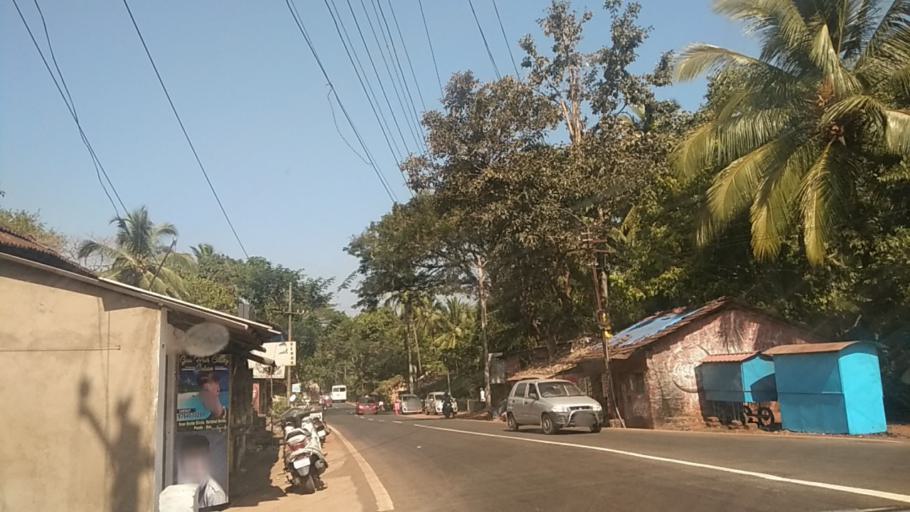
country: IN
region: Goa
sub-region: North Goa
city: Queula
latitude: 15.3542
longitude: 74.0030
